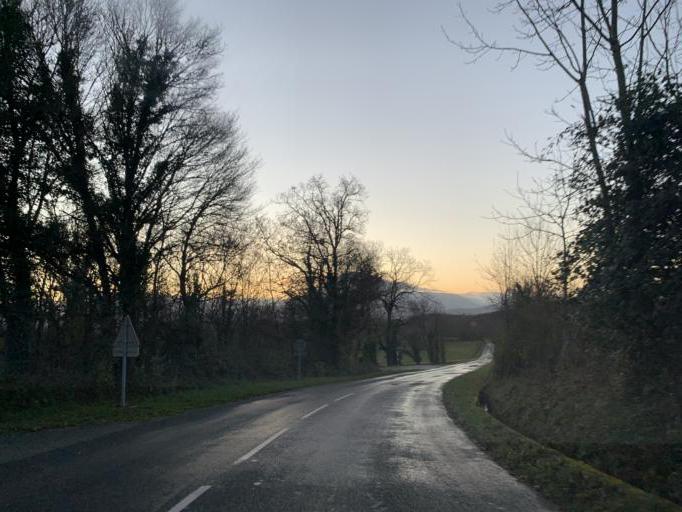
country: FR
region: Rhone-Alpes
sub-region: Departement de l'Ain
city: Belley
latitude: 45.7930
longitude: 5.6425
